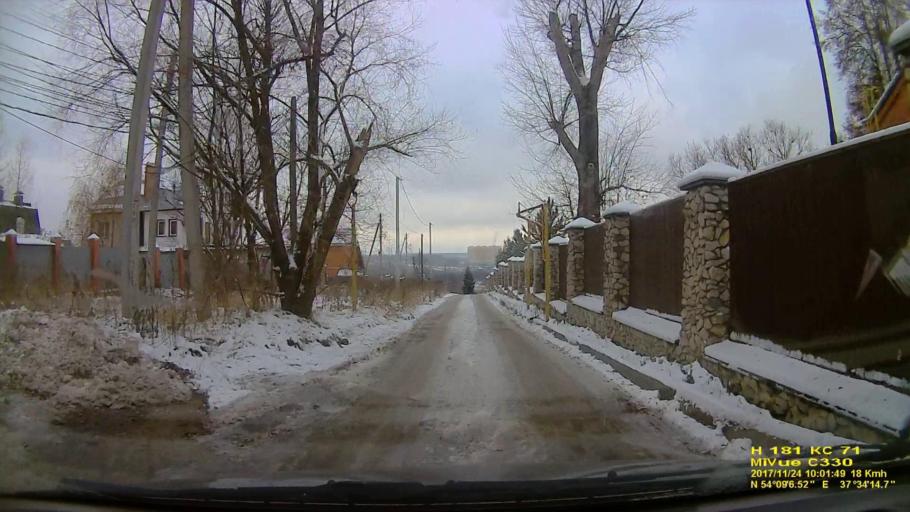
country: RU
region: Tula
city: Mendeleyevskiy
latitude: 54.1519
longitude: 37.5705
